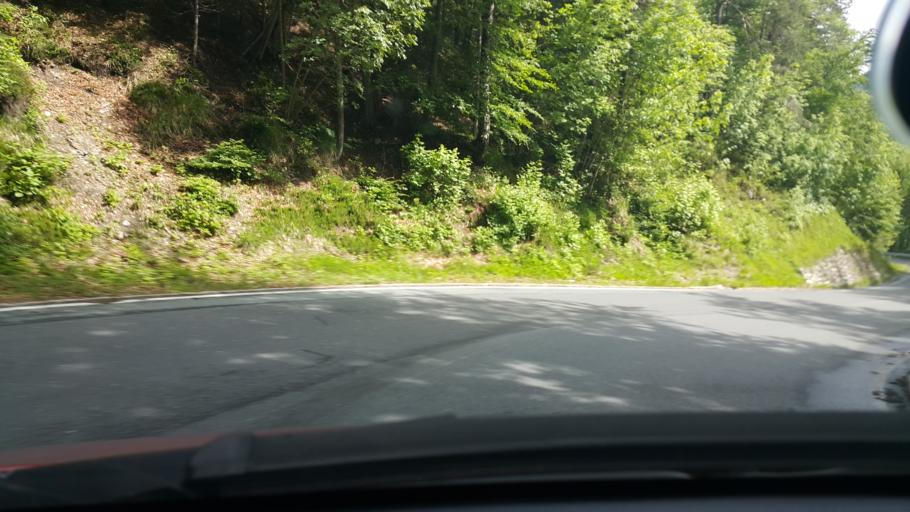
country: AT
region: Carinthia
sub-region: Politischer Bezirk Klagenfurt Land
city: Ferlach
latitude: 46.4940
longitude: 14.2807
